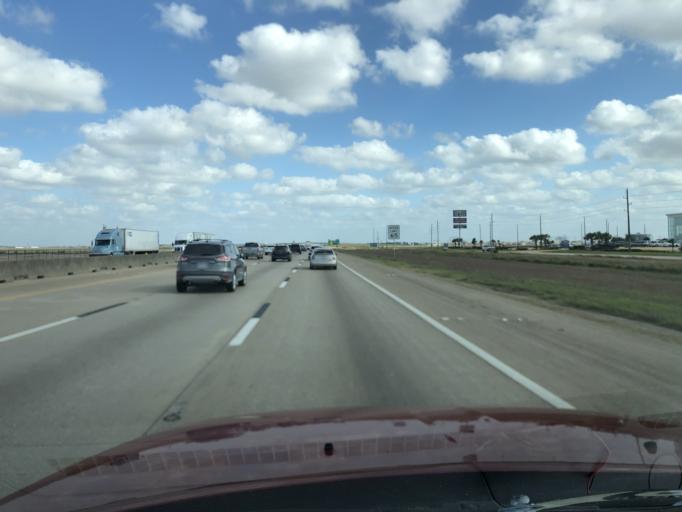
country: US
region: Texas
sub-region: Waller County
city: Brookshire
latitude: 29.7775
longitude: -95.9104
